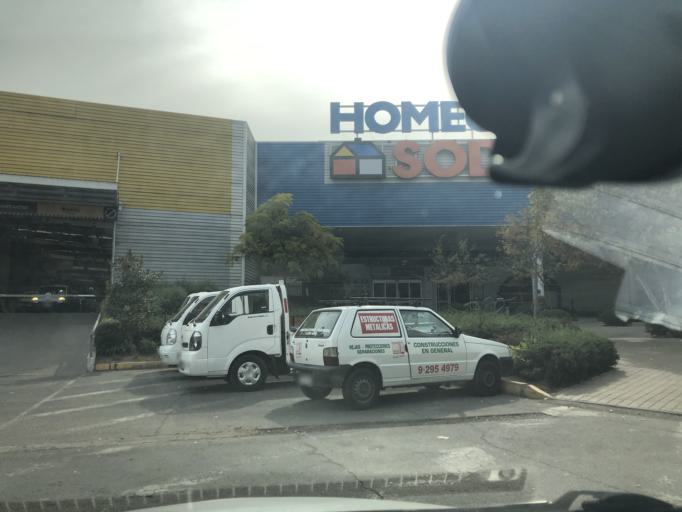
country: CL
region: Santiago Metropolitan
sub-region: Provincia de Cordillera
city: Puente Alto
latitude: -33.5693
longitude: -70.5589
